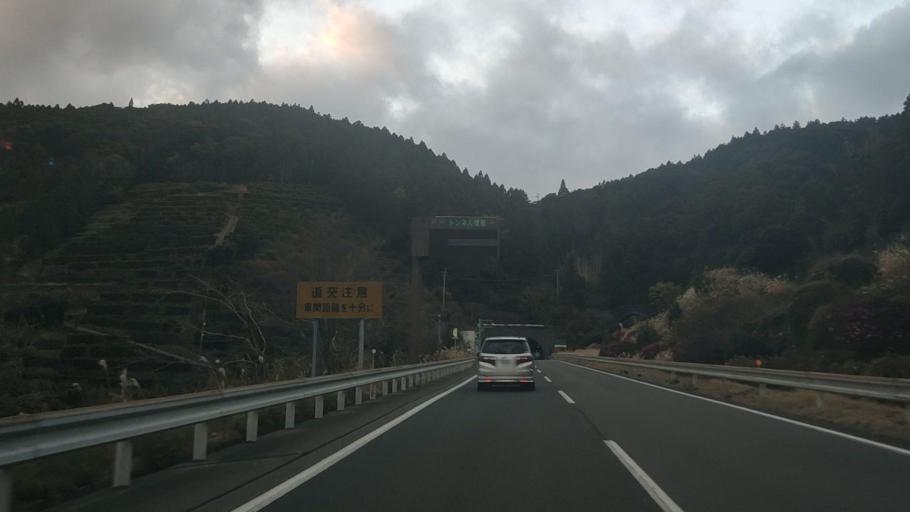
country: JP
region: Nagasaki
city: Obita
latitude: 32.8119
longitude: 129.9323
